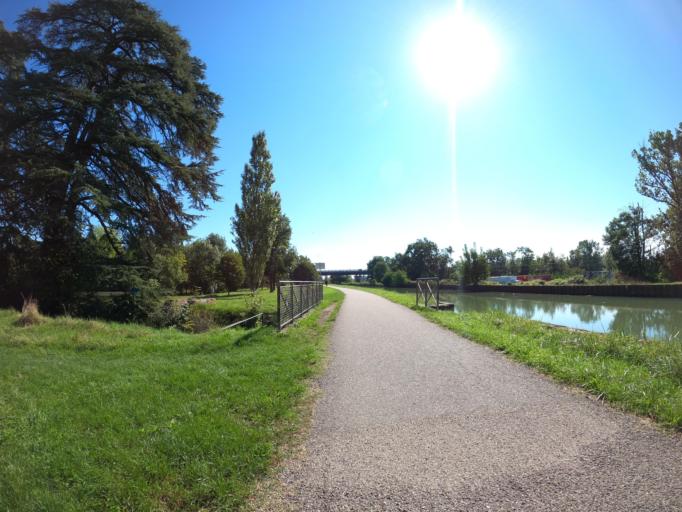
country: FR
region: Aquitaine
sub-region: Departement du Lot-et-Garonne
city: Bon-Encontre
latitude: 44.1739
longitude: 0.6677
